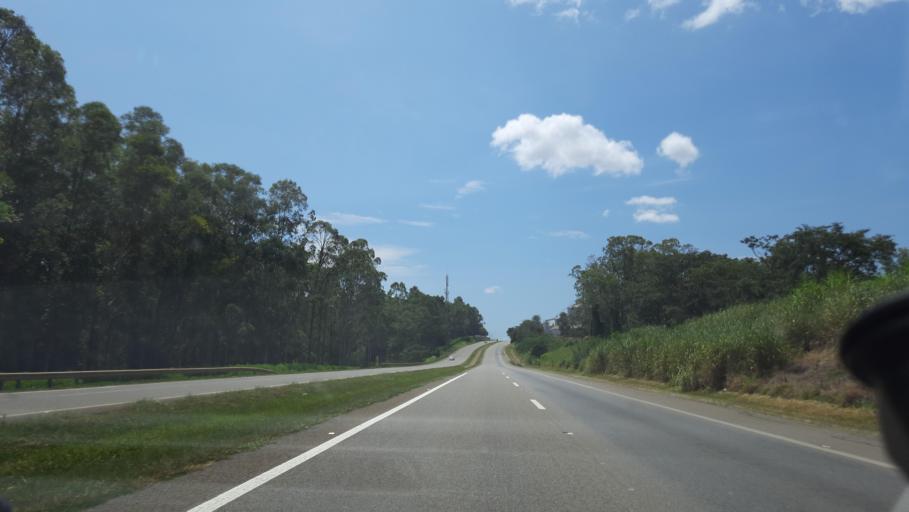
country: BR
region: Sao Paulo
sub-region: Mococa
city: Mococa
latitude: -21.5277
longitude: -47.0288
